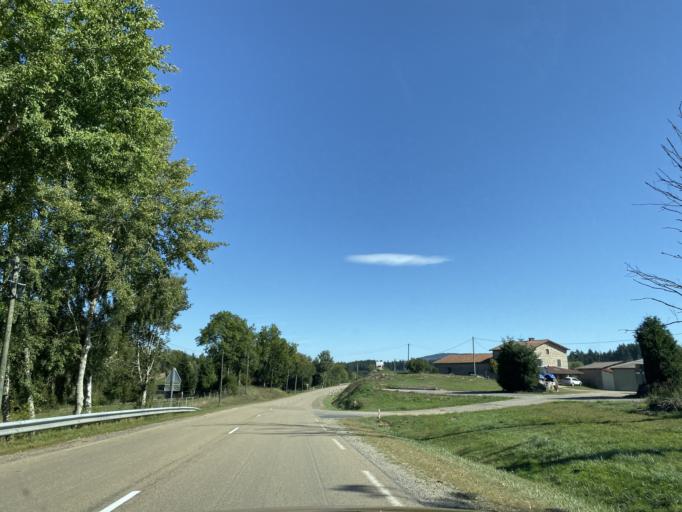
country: FR
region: Rhone-Alpes
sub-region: Departement de la Loire
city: Noiretable
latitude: 45.8294
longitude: 3.7786
